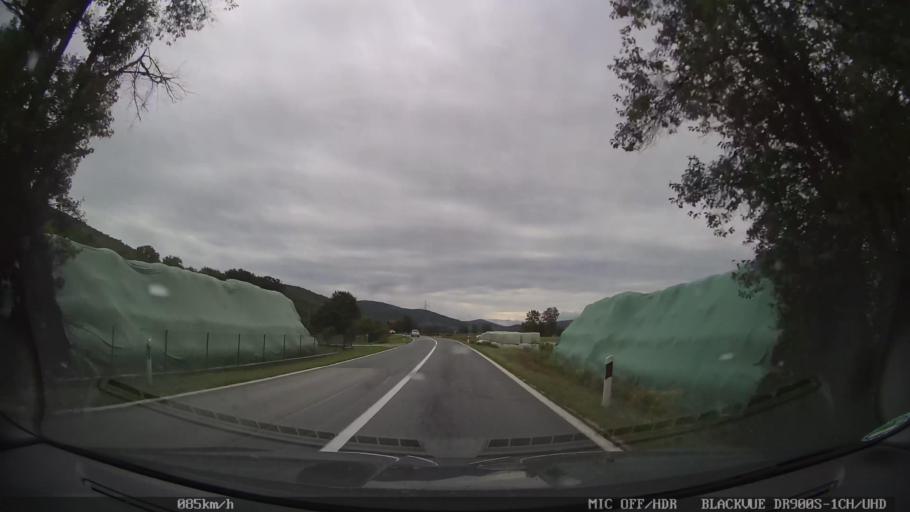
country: HR
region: Licko-Senjska
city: Brinje
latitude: 44.9204
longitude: 15.1454
